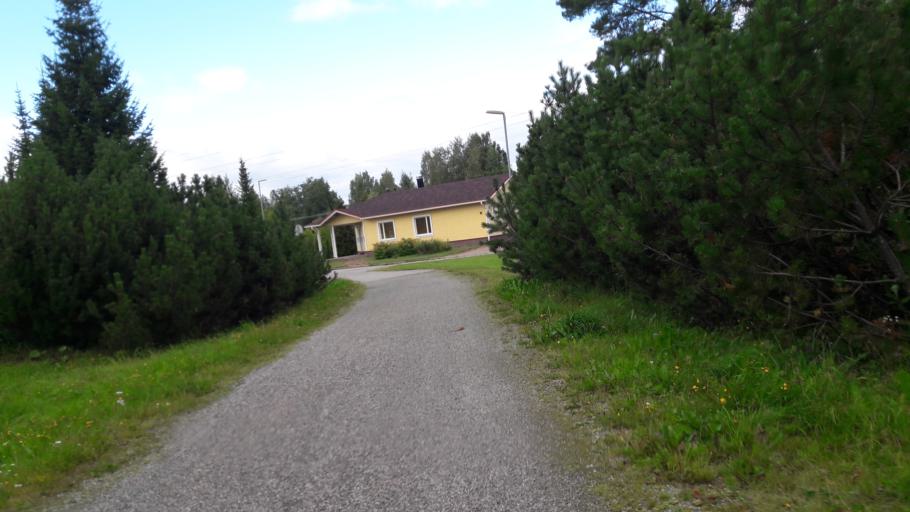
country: FI
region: North Karelia
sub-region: Joensuu
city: Joensuu
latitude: 62.5954
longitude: 29.7958
